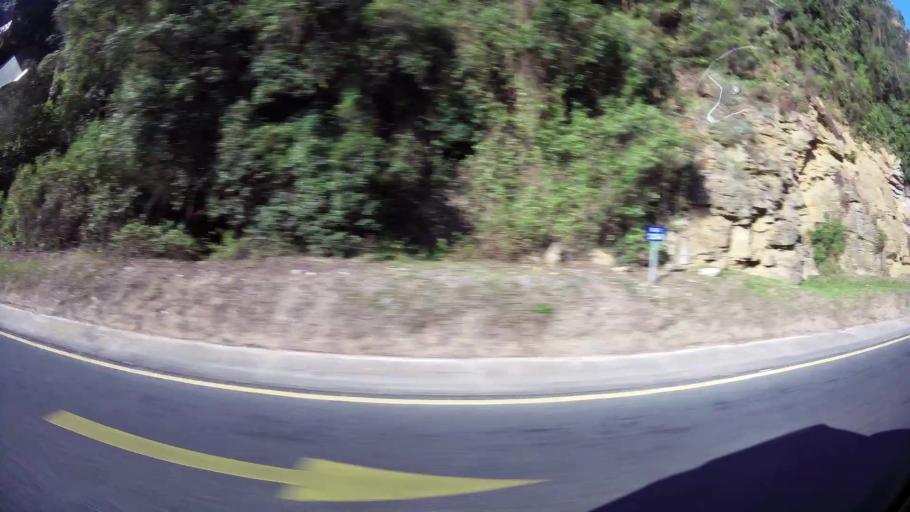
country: ZA
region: Western Cape
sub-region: Eden District Municipality
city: George
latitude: -33.9912
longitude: 22.5520
